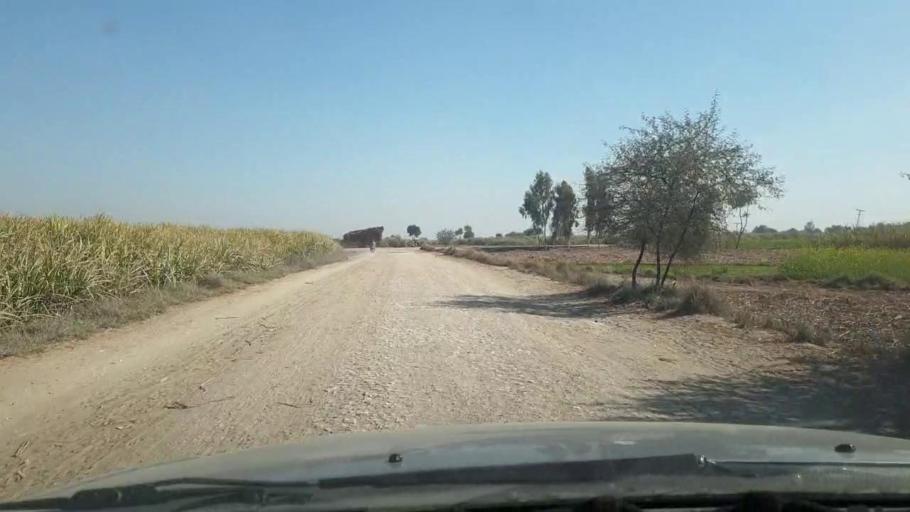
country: PK
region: Sindh
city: Ghotki
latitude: 28.0271
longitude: 69.2180
